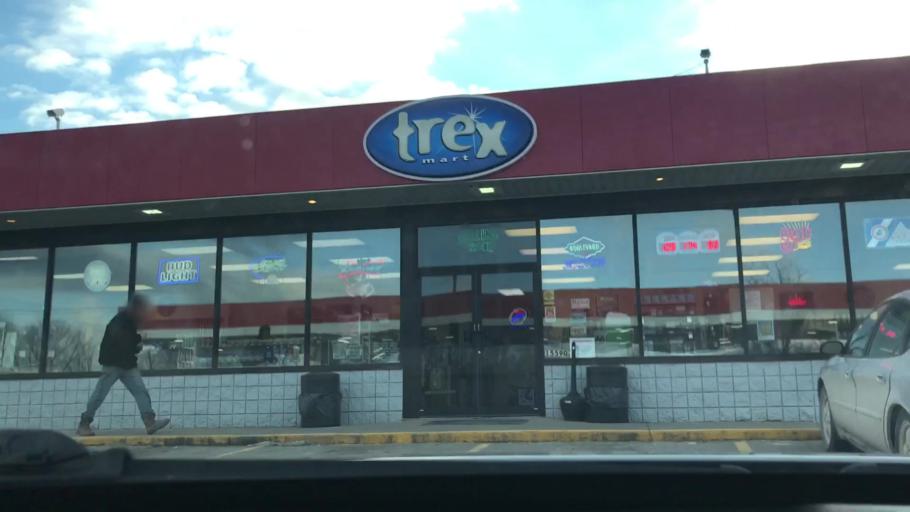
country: US
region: Missouri
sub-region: Platte County
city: Platte City
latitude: 39.3749
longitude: -94.7926
